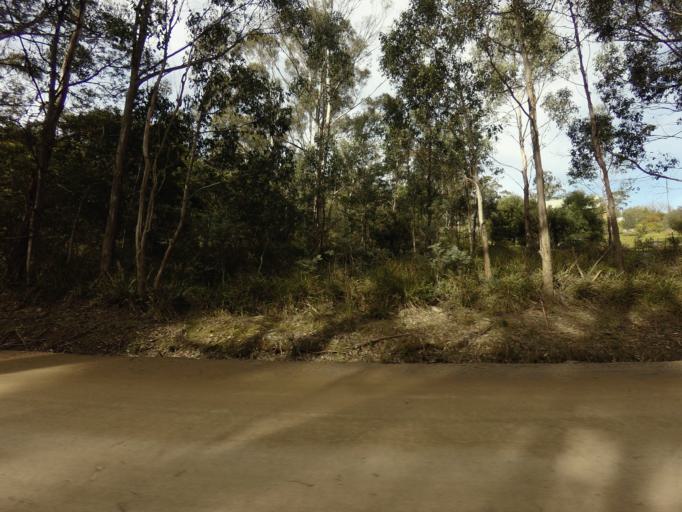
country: AU
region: Tasmania
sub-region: Huon Valley
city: Huonville
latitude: -43.0703
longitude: 147.0867
